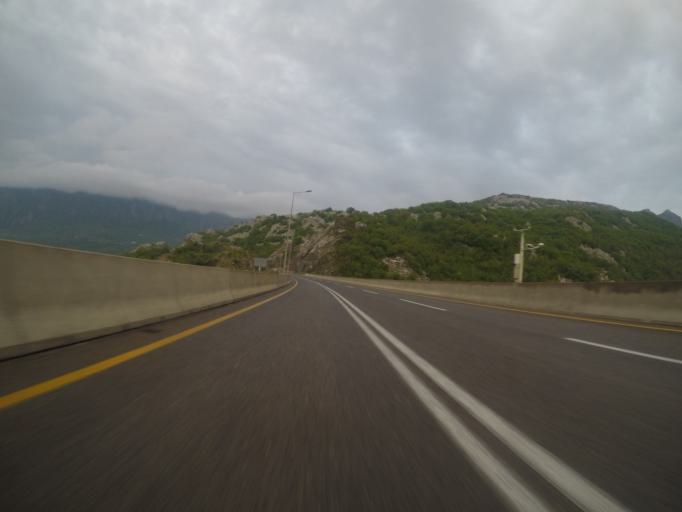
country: ME
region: Bar
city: Sutomore
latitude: 42.2256
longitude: 19.0520
